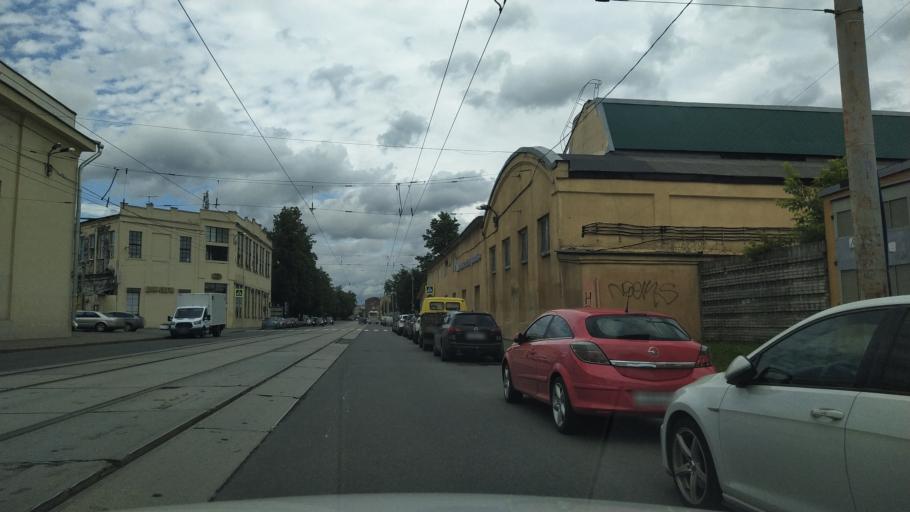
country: RU
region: Leningrad
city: Finlyandskiy
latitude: 59.9581
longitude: 30.3741
